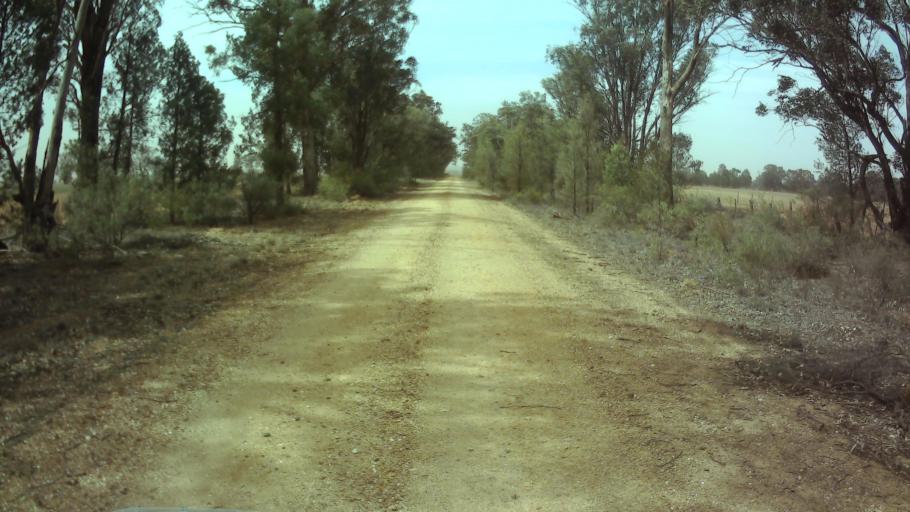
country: AU
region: New South Wales
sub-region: Weddin
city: Grenfell
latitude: -33.7139
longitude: 147.9699
